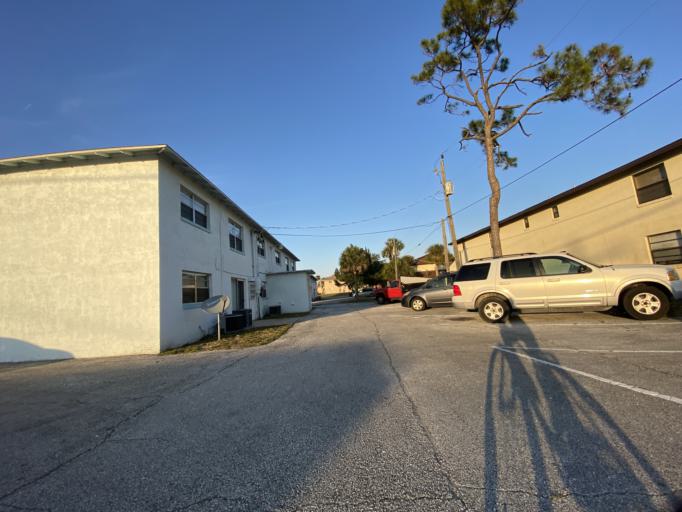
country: US
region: Florida
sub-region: Volusia County
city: South Daytona
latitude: 29.1811
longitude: -81.0098
